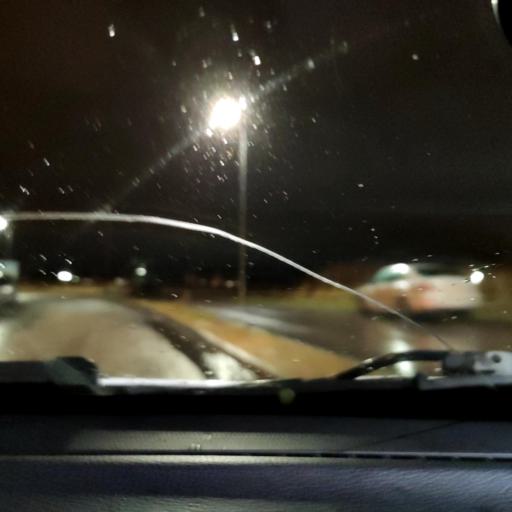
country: RU
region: Tatarstan
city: Osinovo
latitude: 55.8638
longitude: 48.8721
